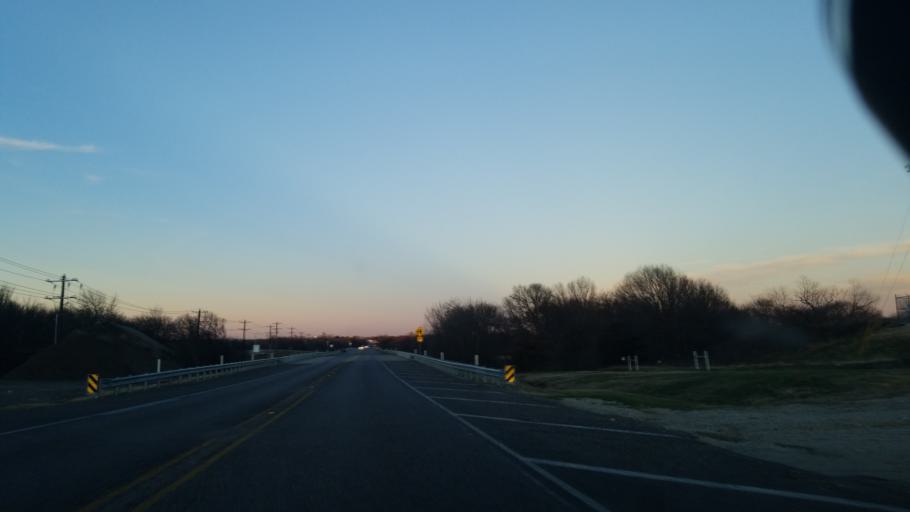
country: US
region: Texas
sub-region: Denton County
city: Argyle
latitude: 33.1620
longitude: -97.1596
